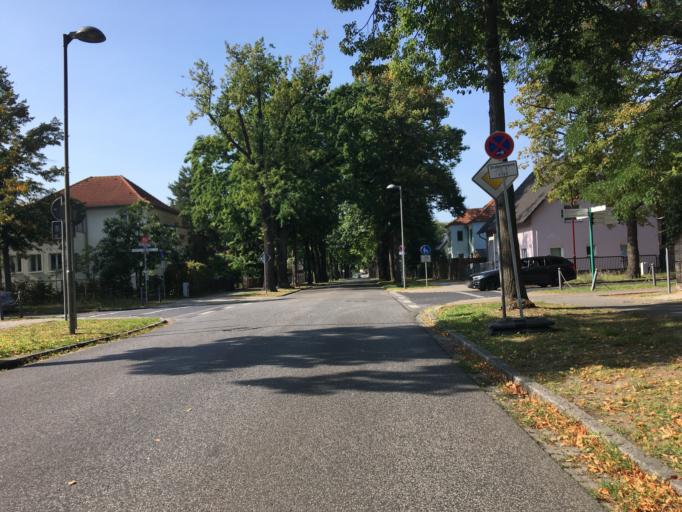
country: DE
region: Brandenburg
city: Zeuthen
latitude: 52.3679
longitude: 13.6245
